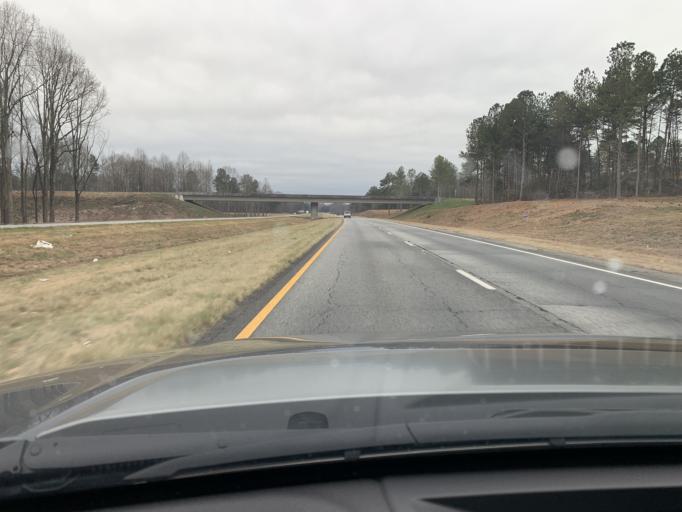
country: US
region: Georgia
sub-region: Habersham County
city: Cornelia
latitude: 34.5160
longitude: -83.5525
